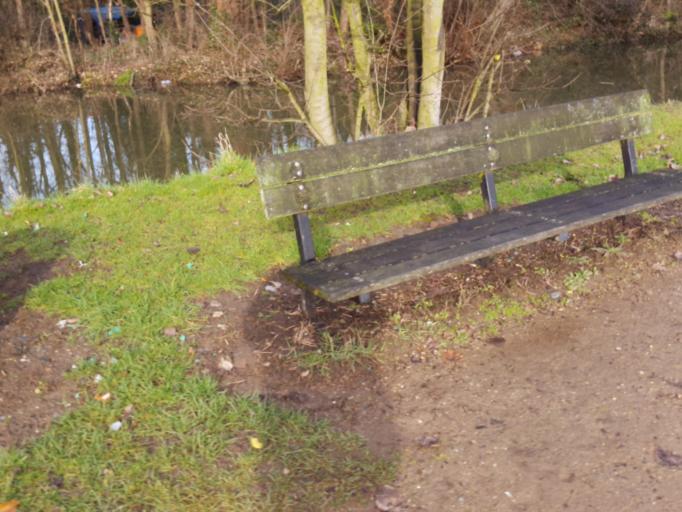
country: GB
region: England
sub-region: Essex
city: Harlow
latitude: 51.7832
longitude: 0.0981
